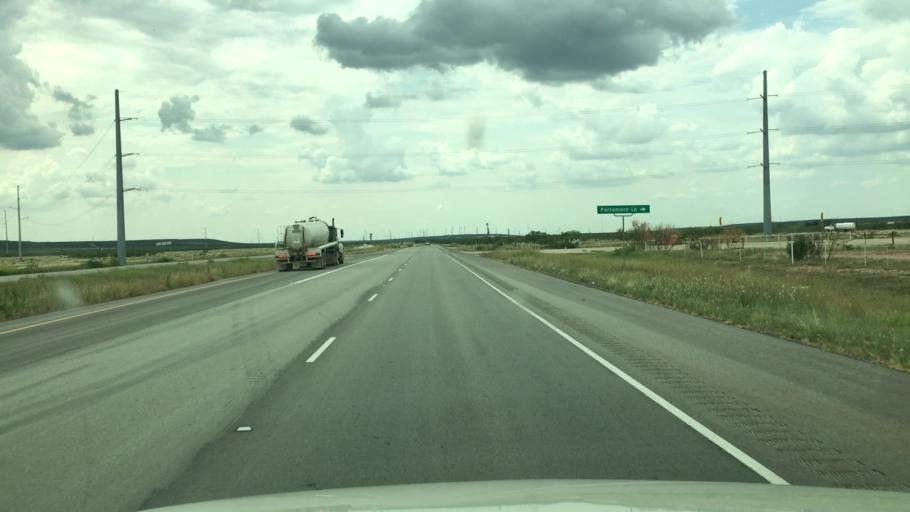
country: US
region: Texas
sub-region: Sterling County
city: Sterling City
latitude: 31.9606
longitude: -101.2121
